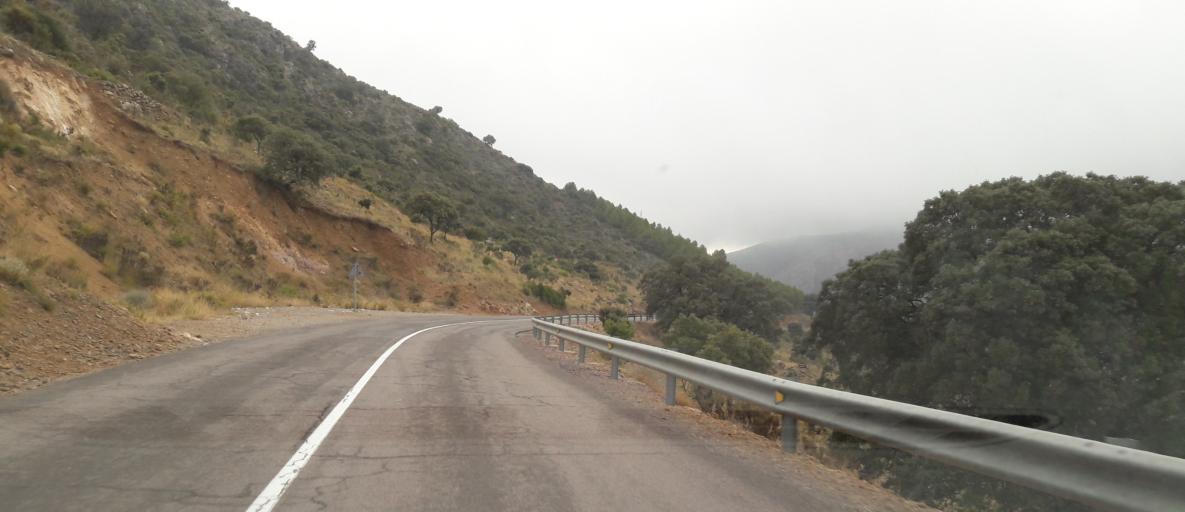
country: ES
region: Andalusia
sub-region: Provincia de Almeria
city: Enix
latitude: 36.8920
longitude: -2.6194
